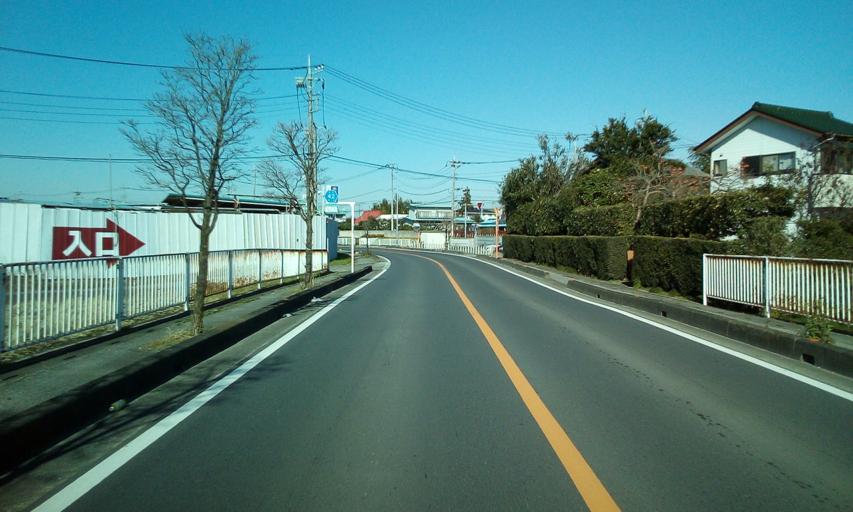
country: JP
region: Chiba
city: Noda
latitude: 35.9710
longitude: 139.8122
